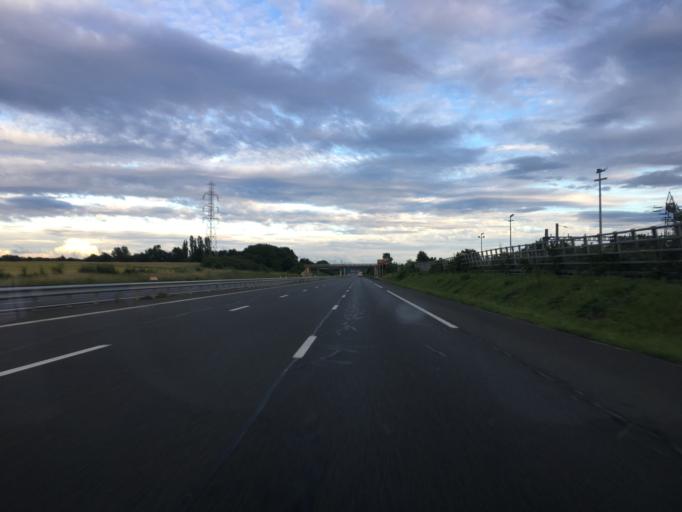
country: FR
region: Ile-de-France
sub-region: Departement de Seine-et-Marne
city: Moisenay
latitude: 48.5714
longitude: 2.7515
